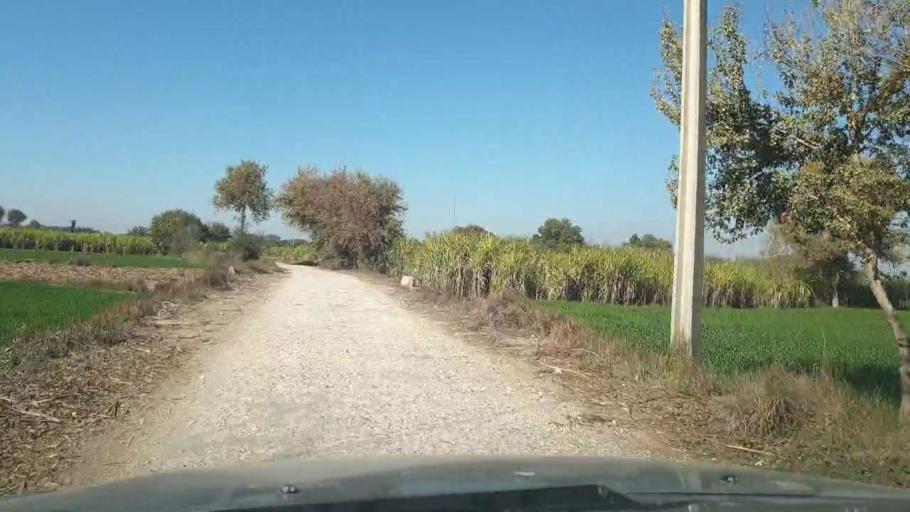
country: PK
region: Sindh
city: Ghotki
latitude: 28.0540
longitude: 69.2411
